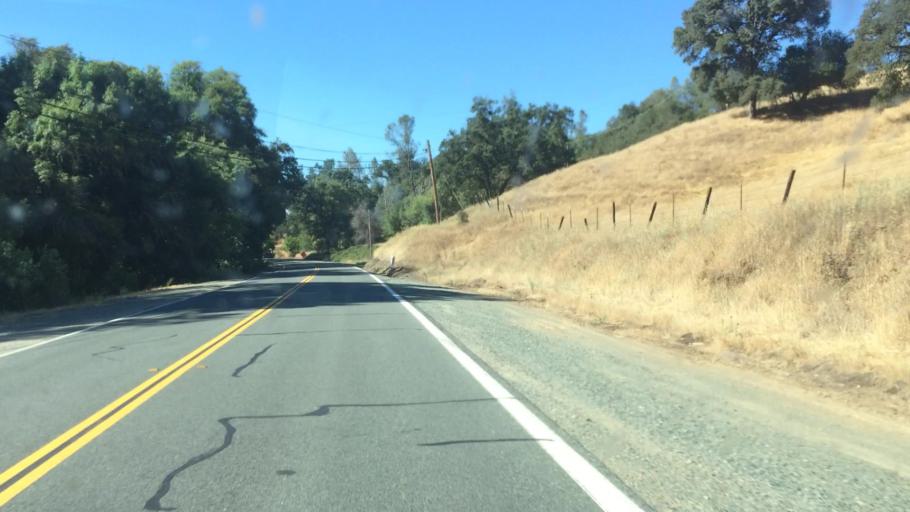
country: US
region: California
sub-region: Amador County
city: Plymouth
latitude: 38.5309
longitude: -120.8473
